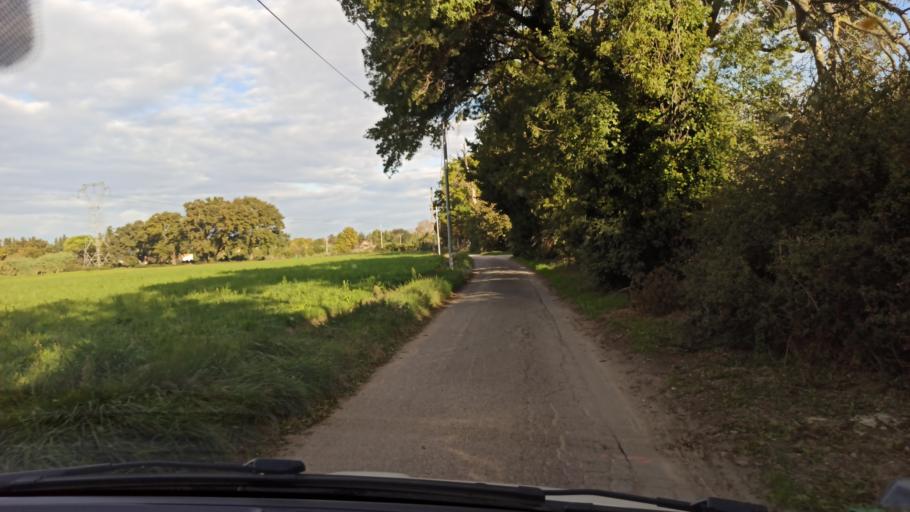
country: FR
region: Provence-Alpes-Cote d'Azur
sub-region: Departement du Vaucluse
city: Montfavet
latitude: 43.9393
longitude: 4.8592
